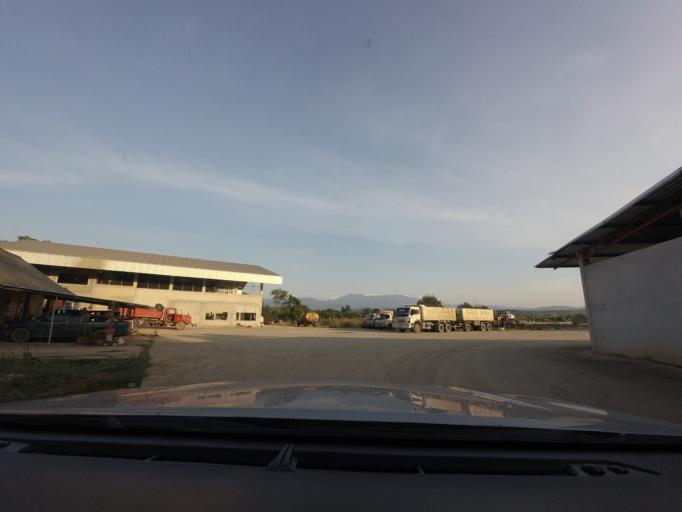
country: TH
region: Chiang Mai
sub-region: Amphoe Chiang Dao
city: Chiang Dao
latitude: 19.3362
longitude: 98.9605
